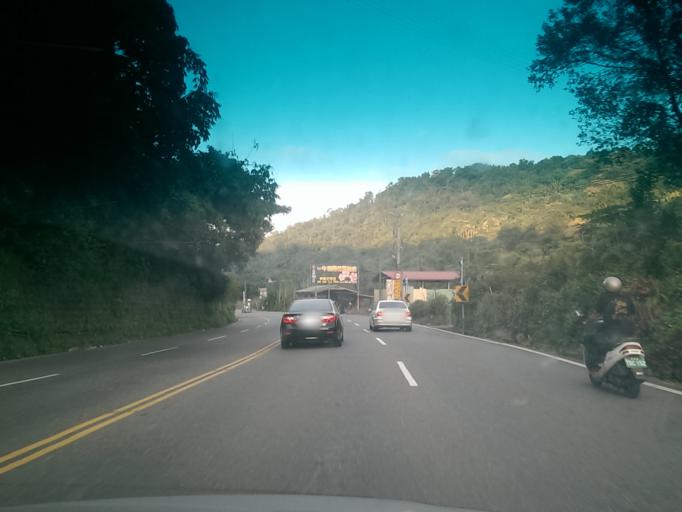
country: TW
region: Taiwan
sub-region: Nantou
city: Puli
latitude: 23.9563
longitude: 120.9422
